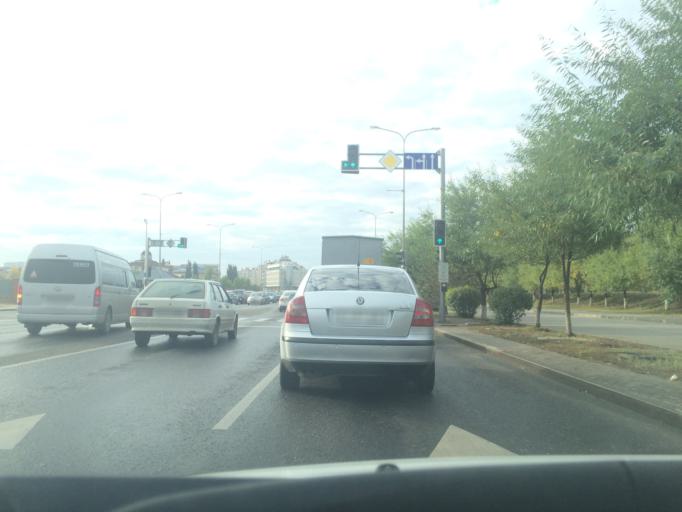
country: KZ
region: Astana Qalasy
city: Astana
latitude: 51.1489
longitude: 71.4446
